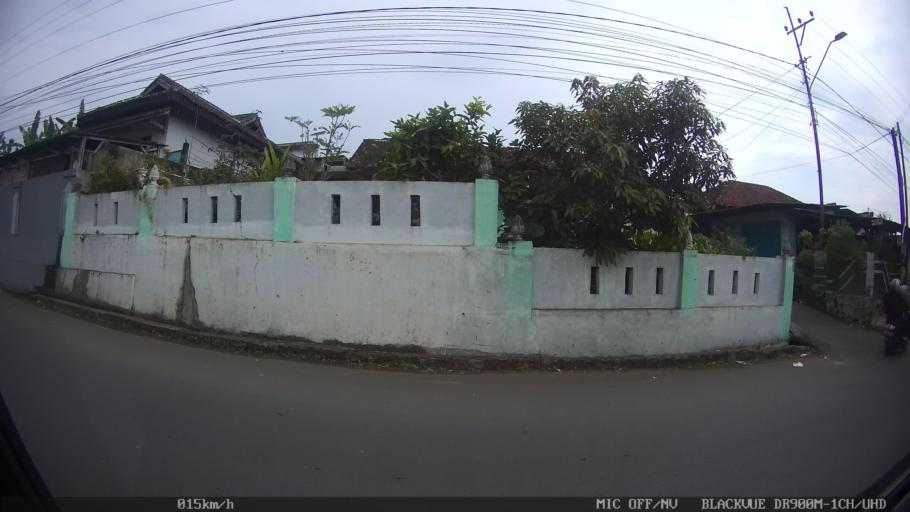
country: ID
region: Lampung
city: Kedaton
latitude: -5.3920
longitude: 105.2138
